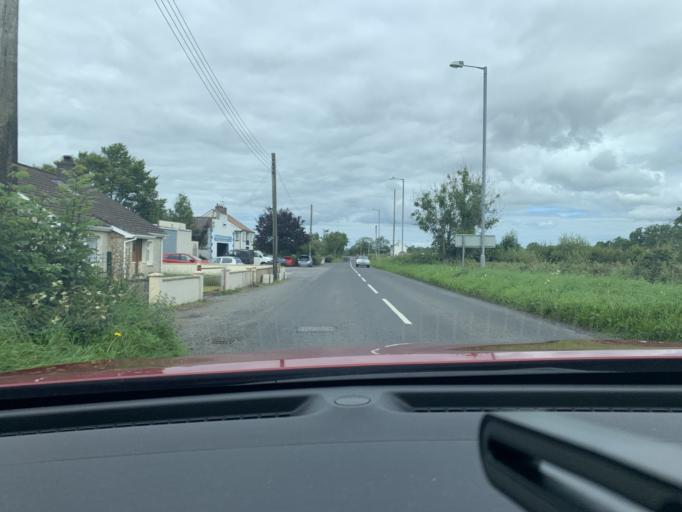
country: GB
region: Northern Ireland
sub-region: Fermanagh District
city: Enniskillen
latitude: 54.2692
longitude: -7.7051
